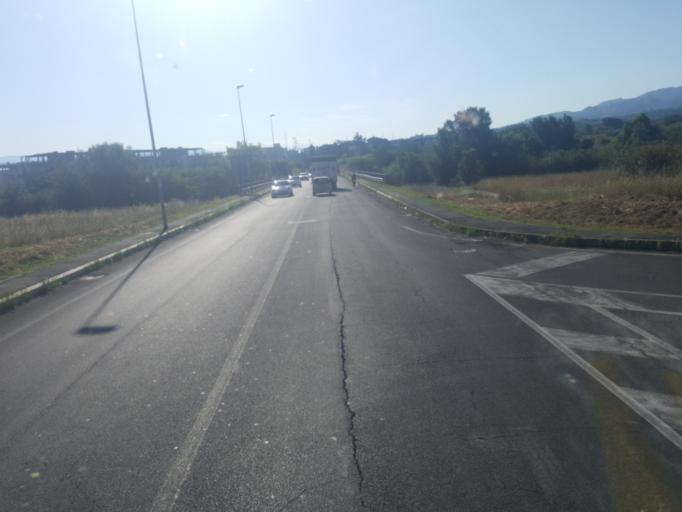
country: IT
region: Latium
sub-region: Citta metropolitana di Roma Capitale
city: Frascati
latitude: 41.8422
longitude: 12.6486
